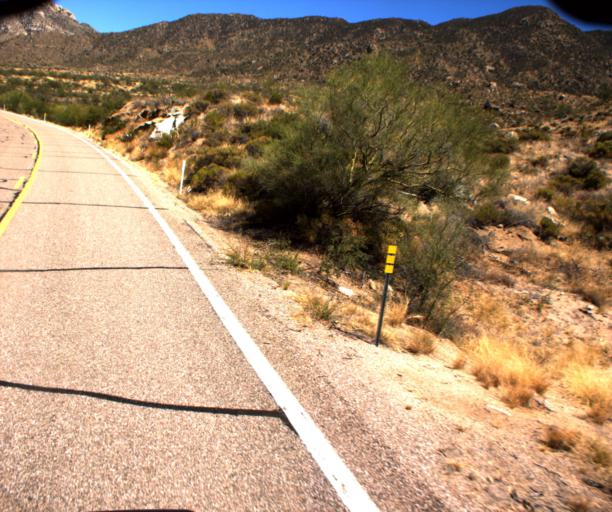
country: US
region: Arizona
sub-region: Pima County
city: Three Points
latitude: 31.9904
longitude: -111.5824
